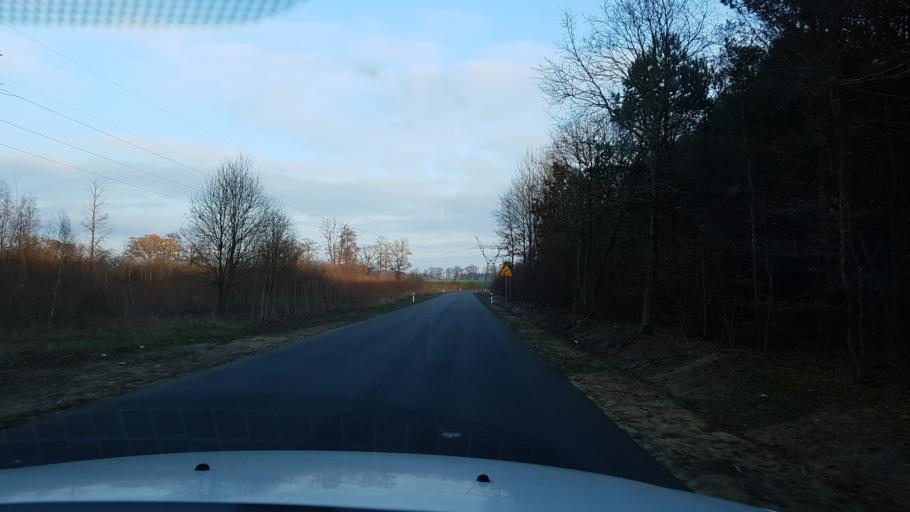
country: PL
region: West Pomeranian Voivodeship
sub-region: Koszalin
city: Koszalin
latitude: 54.1193
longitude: 16.1067
